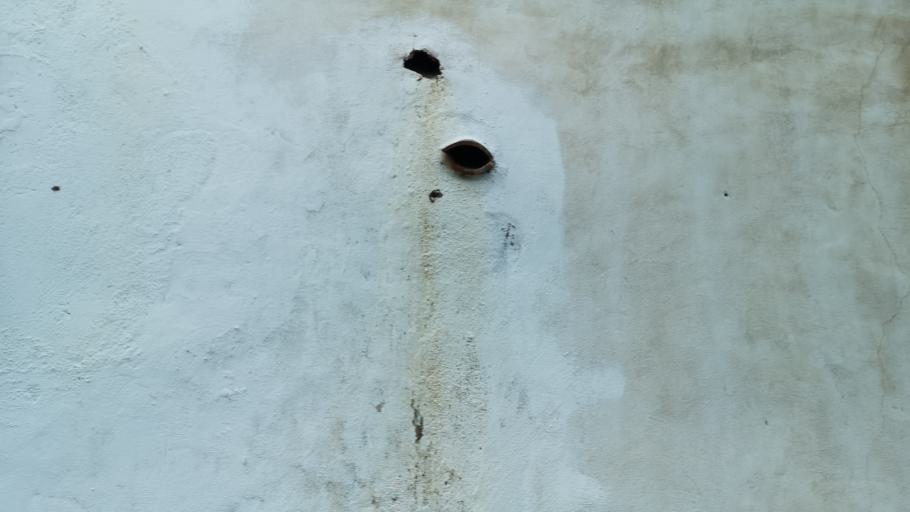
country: ES
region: Canary Islands
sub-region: Provincia de Santa Cruz de Tenerife
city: Vallehermosa
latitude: 28.1803
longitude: -17.2666
